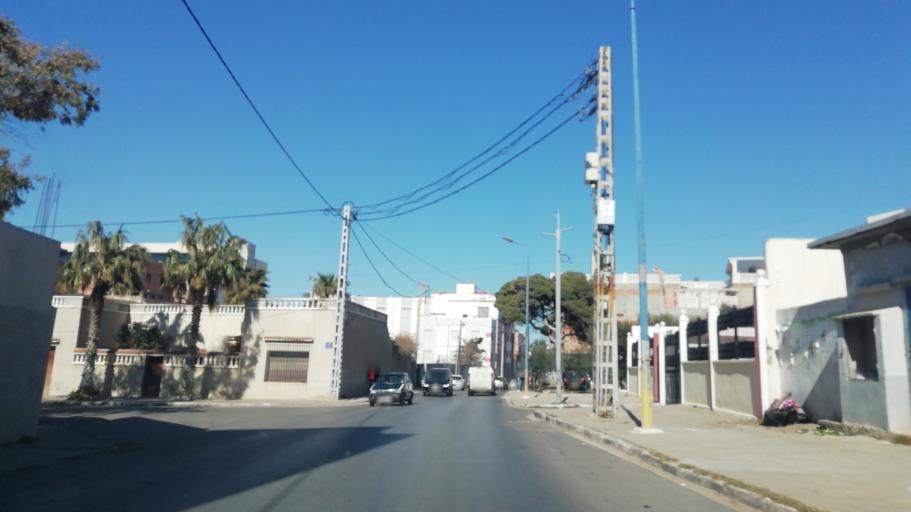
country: DZ
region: Oran
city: Bir el Djir
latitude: 35.7466
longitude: -0.5691
